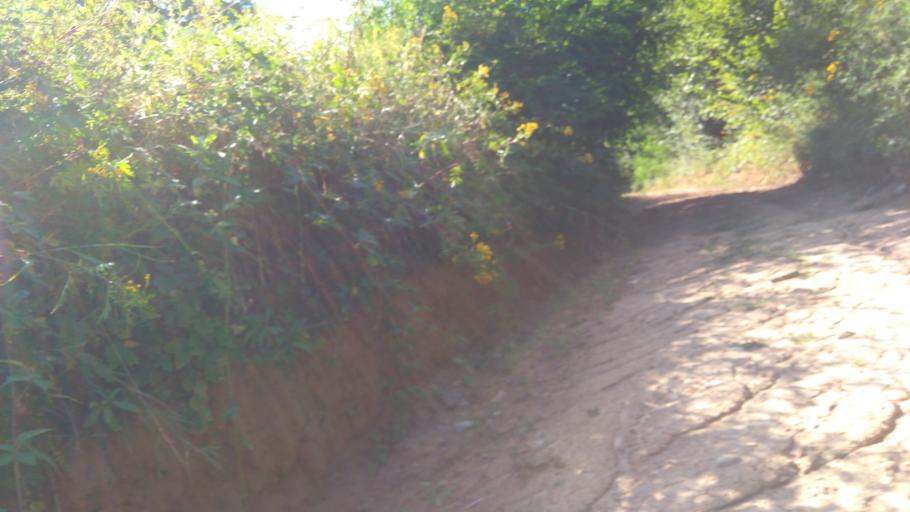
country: SK
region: Nitriansky
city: Sahy
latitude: 47.9893
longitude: 18.9659
